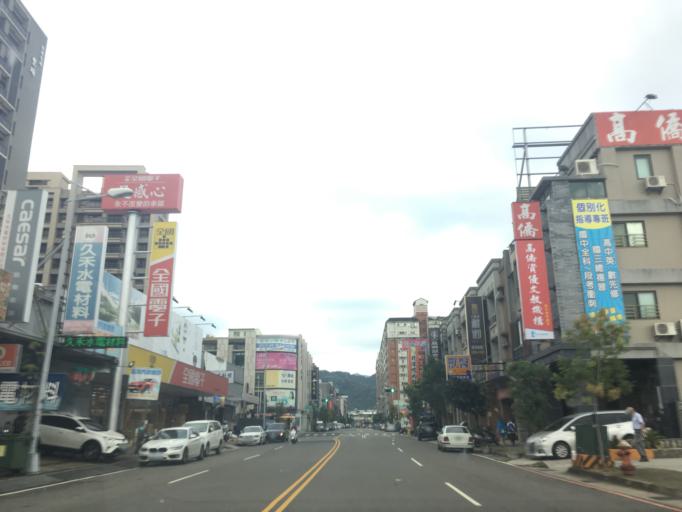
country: TW
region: Taiwan
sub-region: Taichung City
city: Taichung
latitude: 24.1581
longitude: 120.7194
